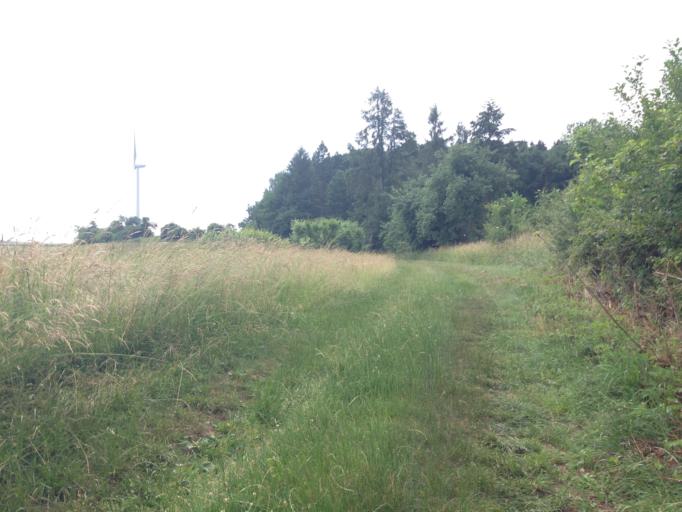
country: DE
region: Hesse
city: Wetter
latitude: 50.8558
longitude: 8.7285
